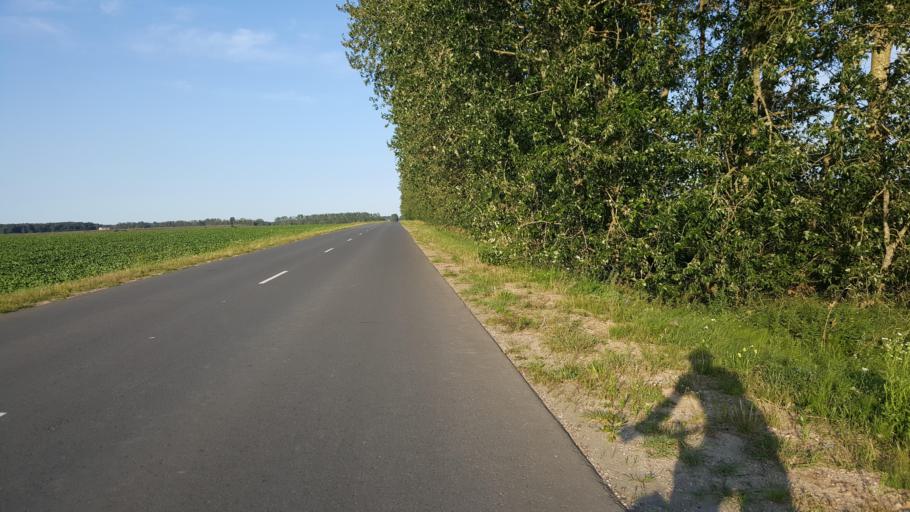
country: BY
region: Brest
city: Vysokaye
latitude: 52.3717
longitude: 23.5736
